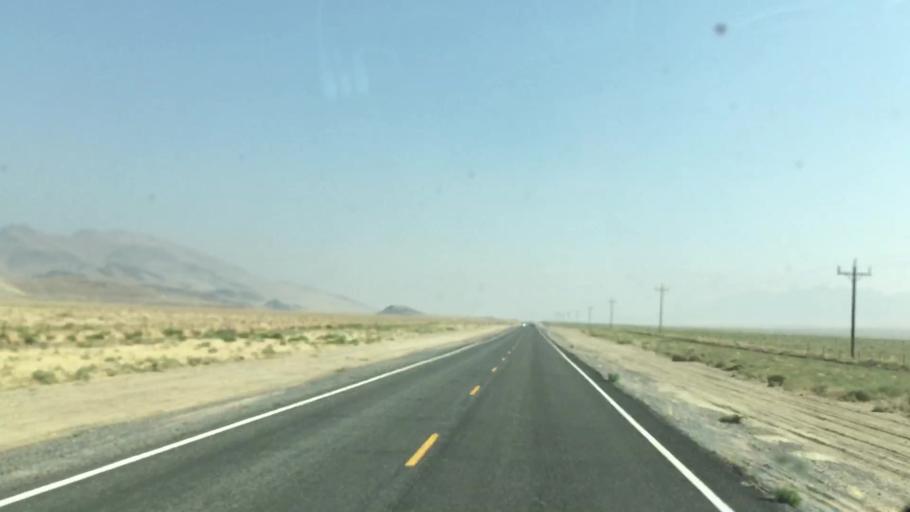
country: US
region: Nevada
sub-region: Lyon County
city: Fernley
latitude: 40.3496
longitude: -119.3390
